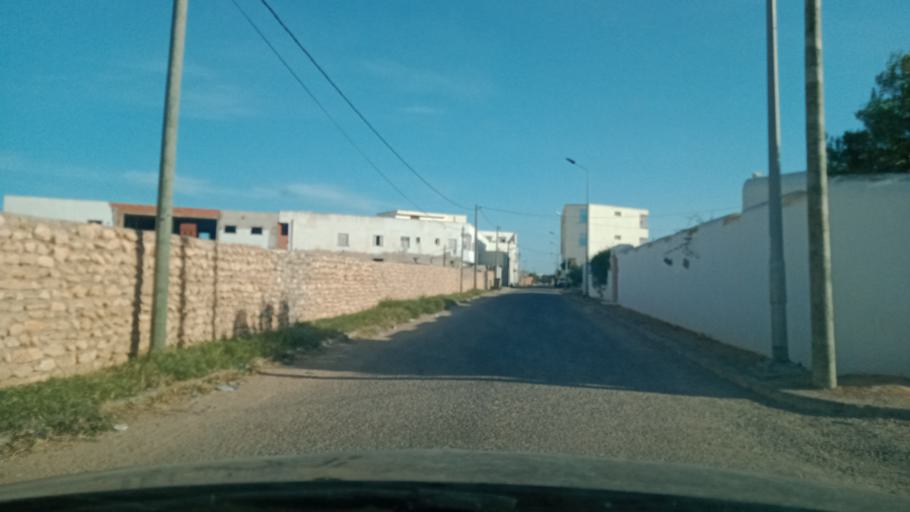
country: TN
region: Safaqis
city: Sfax
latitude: 34.8242
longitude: 10.7357
